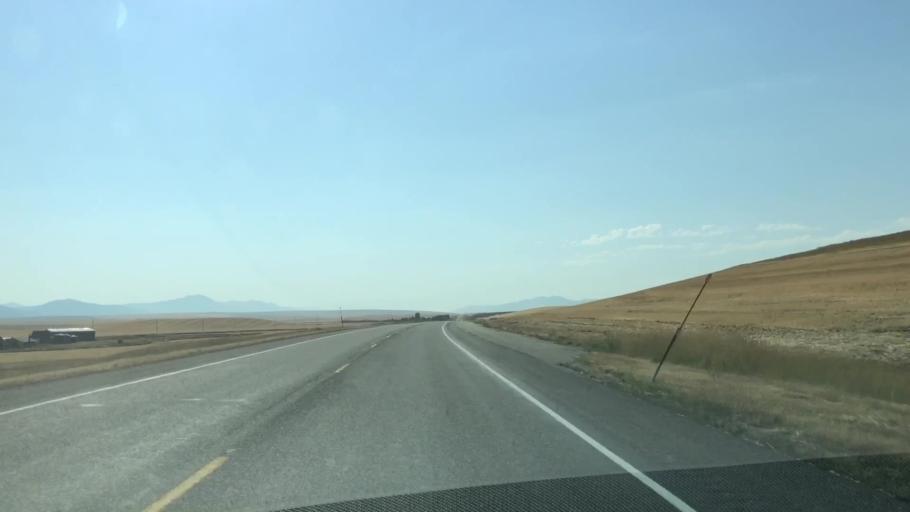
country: US
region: Idaho
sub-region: Madison County
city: Rexburg
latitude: 43.5798
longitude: -111.5684
